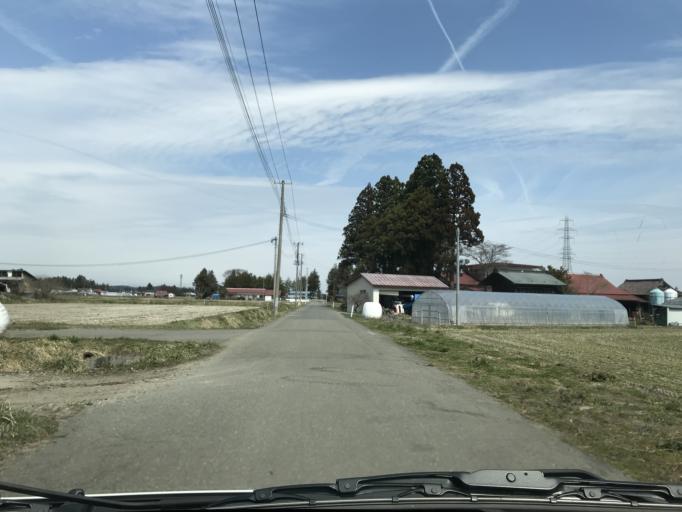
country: JP
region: Iwate
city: Mizusawa
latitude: 39.1307
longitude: 141.0836
